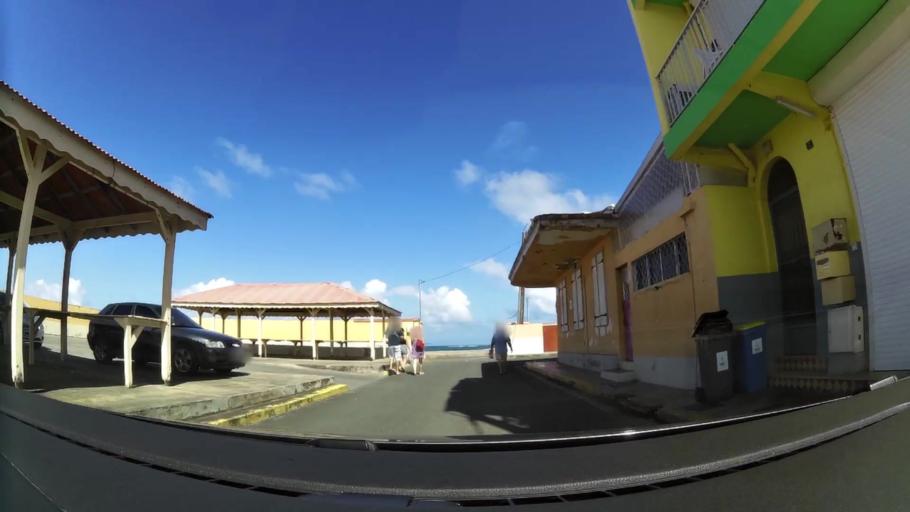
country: GP
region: Guadeloupe
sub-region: Guadeloupe
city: Le Moule
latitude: 16.3324
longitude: -61.3441
